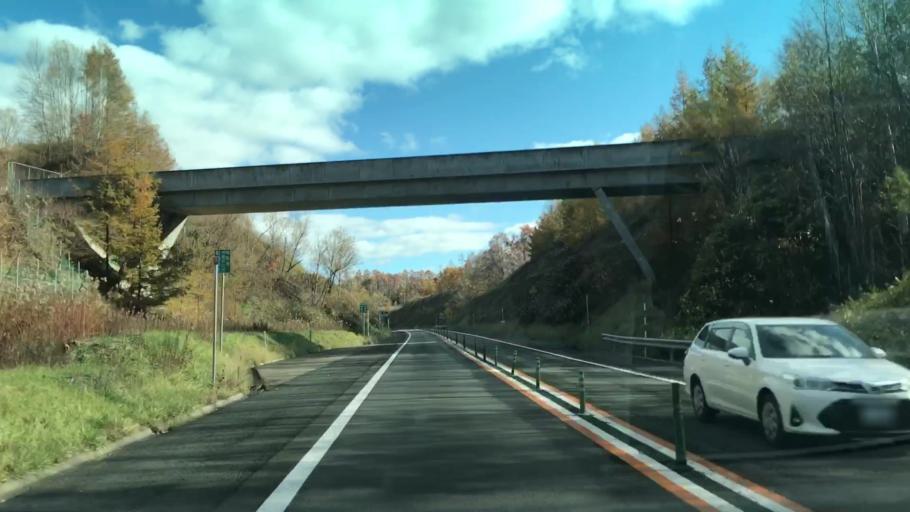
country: JP
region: Hokkaido
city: Chitose
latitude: 42.9133
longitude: 141.9255
